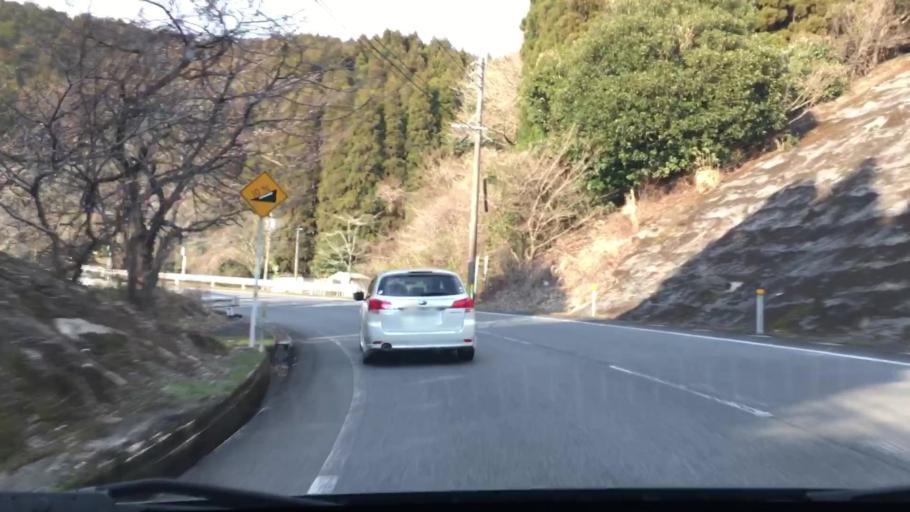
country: JP
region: Miyazaki
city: Miyazaki-shi
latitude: 31.7761
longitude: 131.3330
